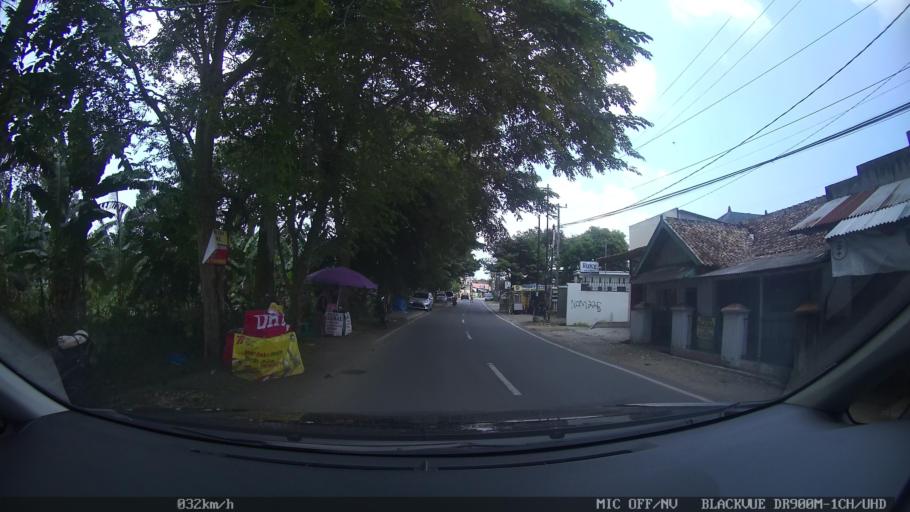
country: ID
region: Lampung
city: Kedaton
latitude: -5.3757
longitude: 105.2660
